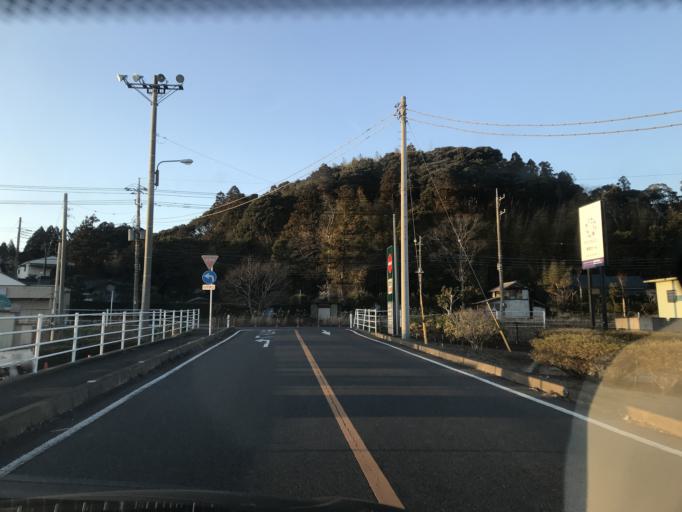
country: JP
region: Chiba
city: Omigawa
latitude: 35.8539
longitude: 140.5875
